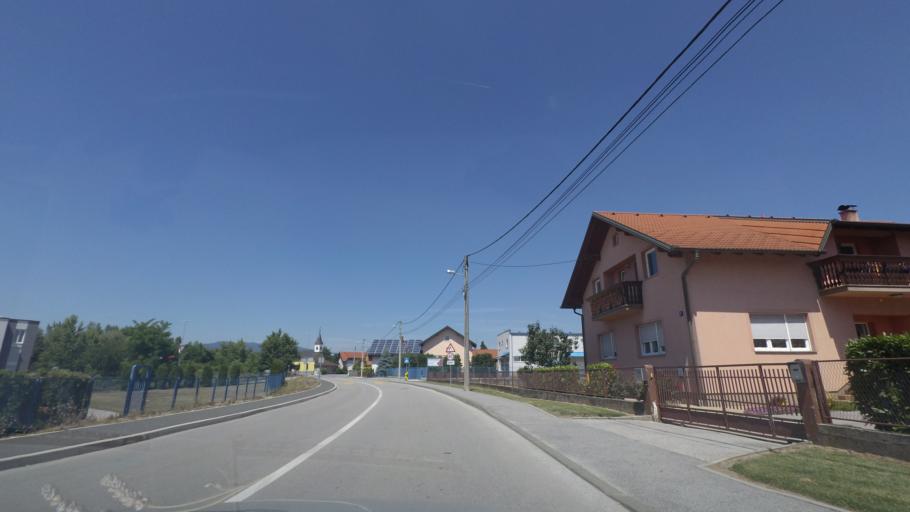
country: HR
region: Grad Zagreb
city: Zadvorsko
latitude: 45.7641
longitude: 15.9188
